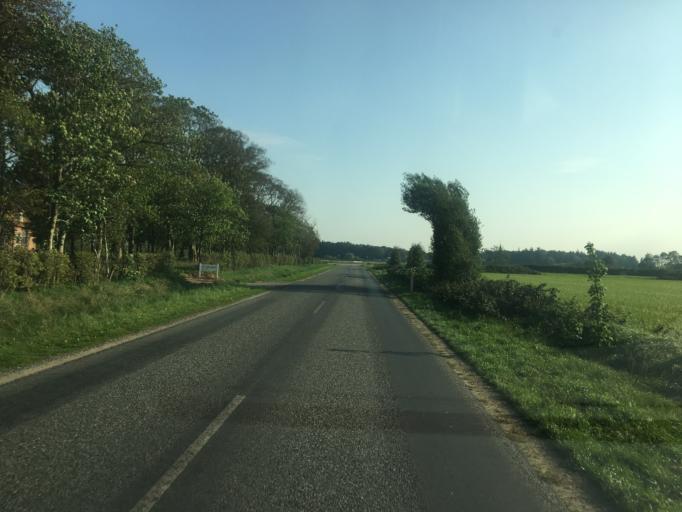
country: DE
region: Schleswig-Holstein
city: Bramstedtlund
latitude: 54.9325
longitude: 9.0679
